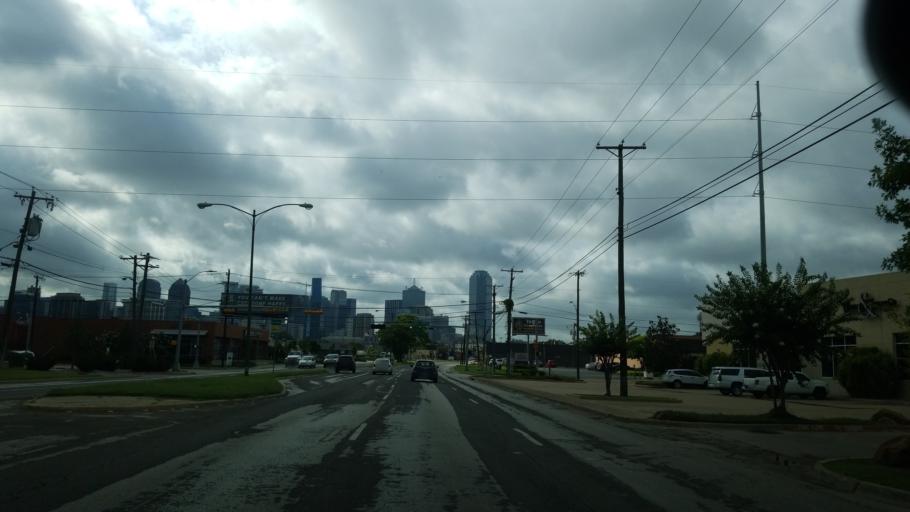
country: US
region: Texas
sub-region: Dallas County
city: Dallas
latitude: 32.7927
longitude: -96.8239
